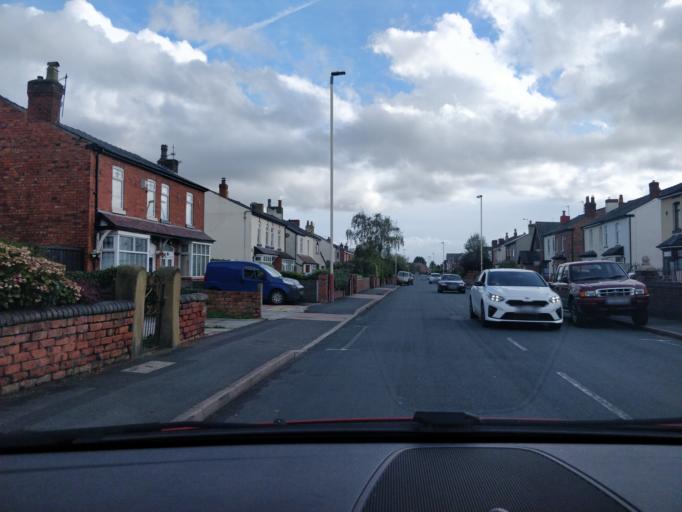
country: GB
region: England
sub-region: Sefton
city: Southport
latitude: 53.6289
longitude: -3.0070
